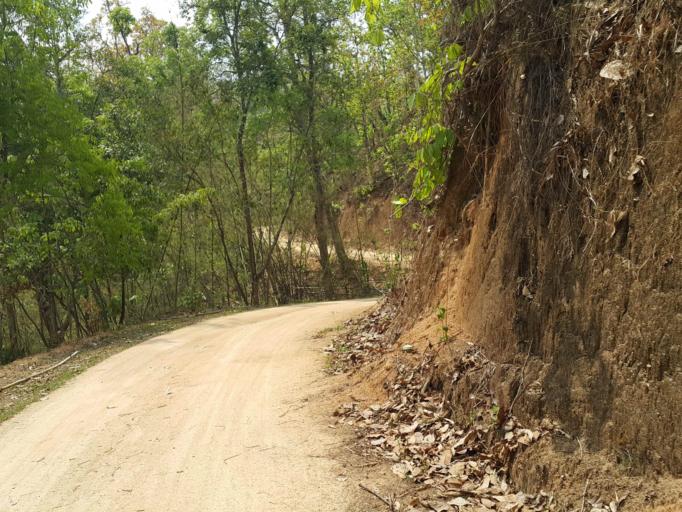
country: TH
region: Chiang Mai
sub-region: Amphoe Chiang Dao
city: Chiang Dao
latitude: 19.3025
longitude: 98.7426
